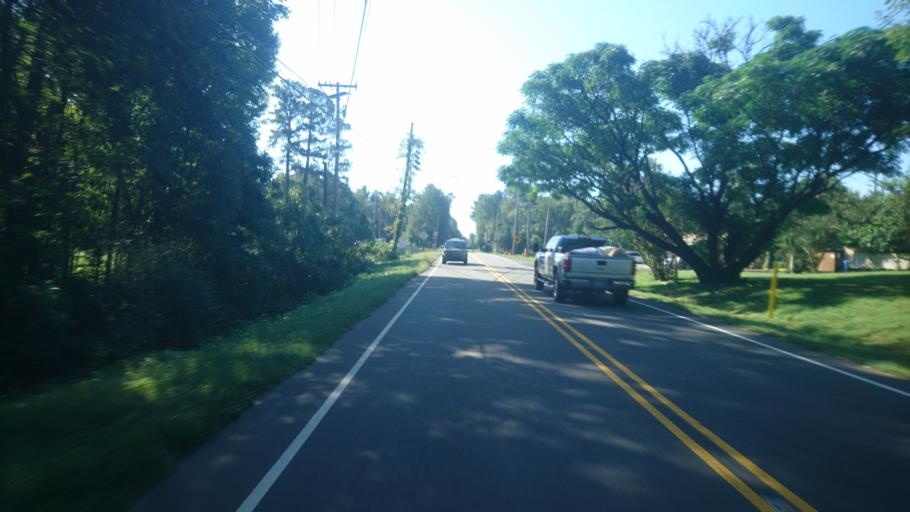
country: US
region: North Carolina
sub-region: Orange County
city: Chapel Hill
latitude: 35.9939
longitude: -79.0721
